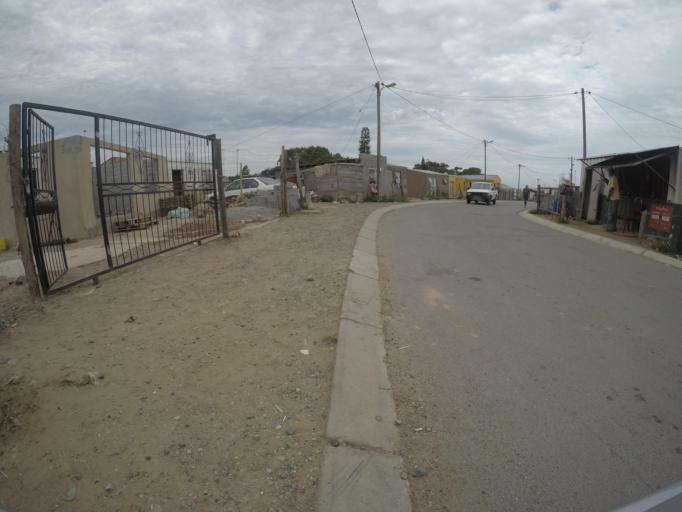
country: ZA
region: Eastern Cape
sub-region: Buffalo City Metropolitan Municipality
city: East London
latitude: -32.9505
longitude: 27.9260
